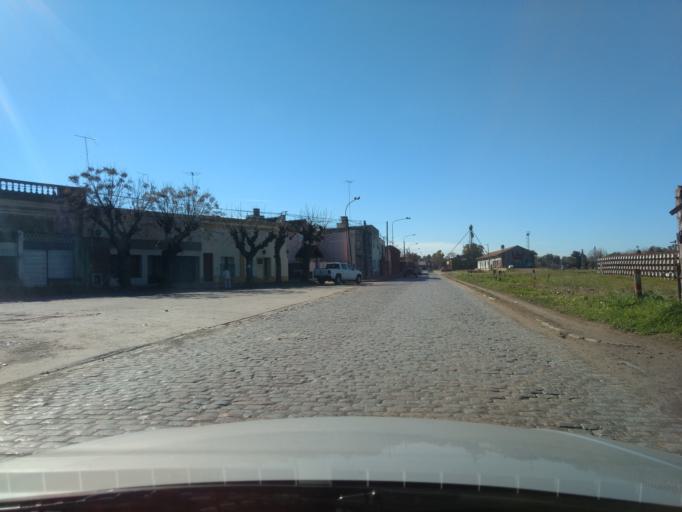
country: AR
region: Buenos Aires
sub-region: Partido de Lujan
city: Lujan
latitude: -34.5769
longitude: -59.1048
